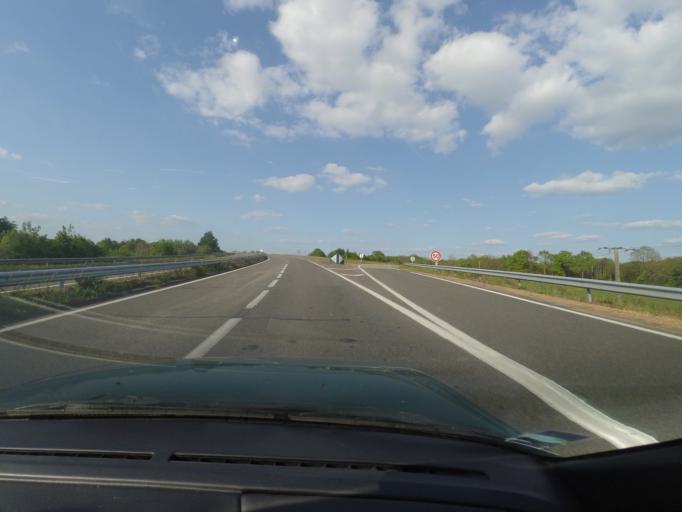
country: FR
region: Pays de la Loire
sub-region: Departement de la Vendee
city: Saligny
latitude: 46.8338
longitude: -1.4214
